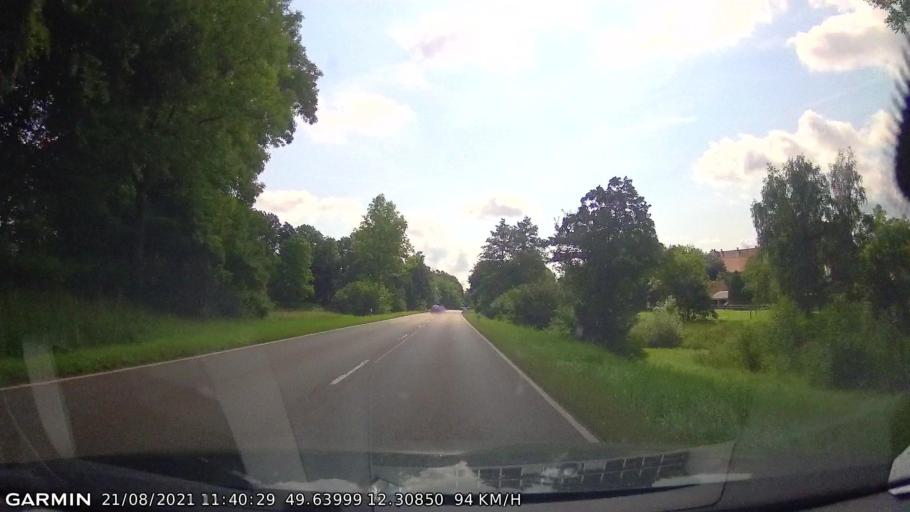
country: DE
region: Bavaria
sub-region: Upper Palatinate
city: Vohenstrauss
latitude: 49.6400
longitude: 12.3085
